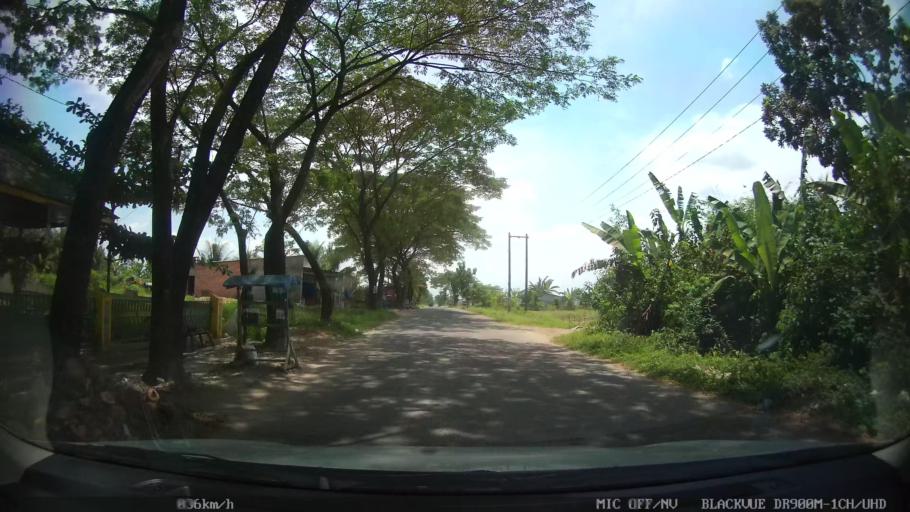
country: ID
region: North Sumatra
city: Binjai
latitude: 3.5912
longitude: 98.5198
